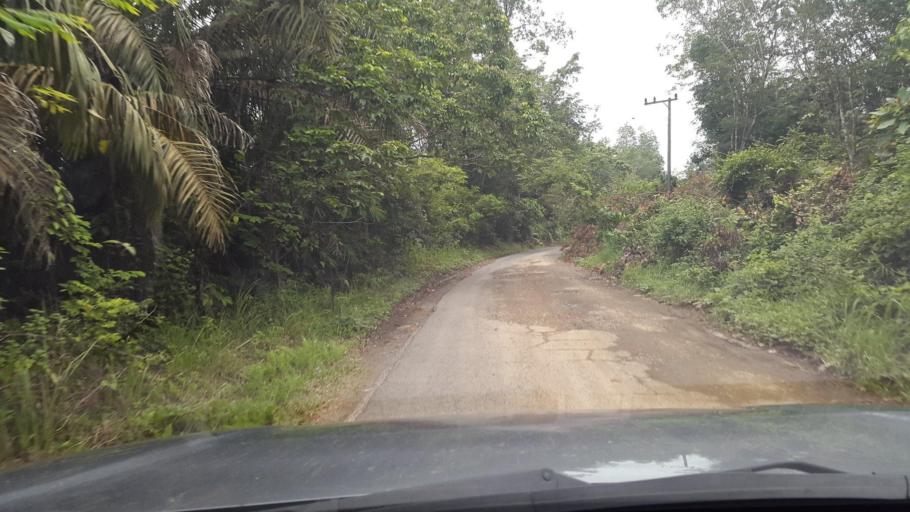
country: ID
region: South Sumatra
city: Sekayu
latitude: -3.1011
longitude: 103.8079
